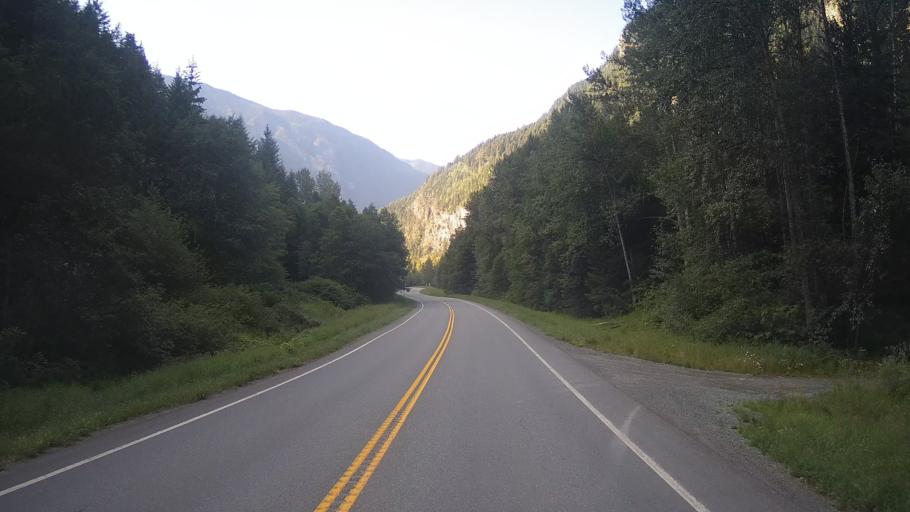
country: CA
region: British Columbia
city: Lillooet
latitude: 50.5918
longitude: -122.0937
